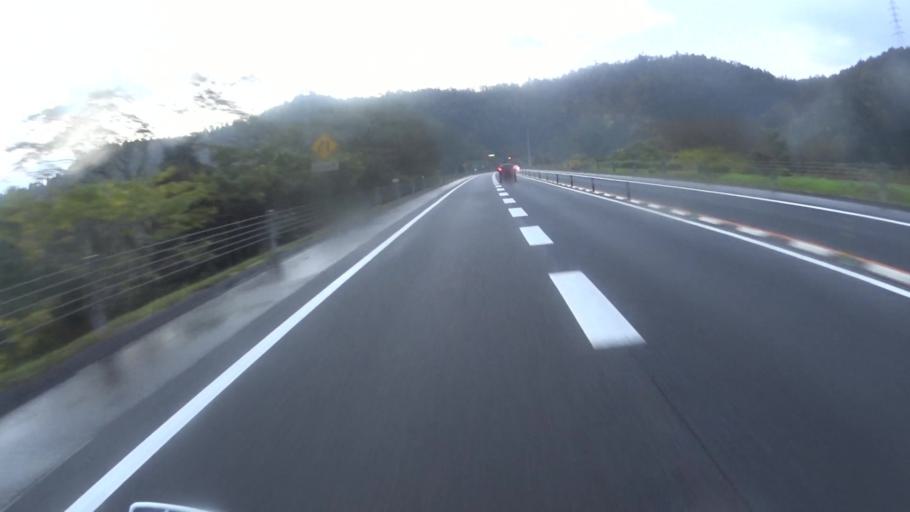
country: JP
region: Kyoto
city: Ayabe
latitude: 35.3813
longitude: 135.2533
